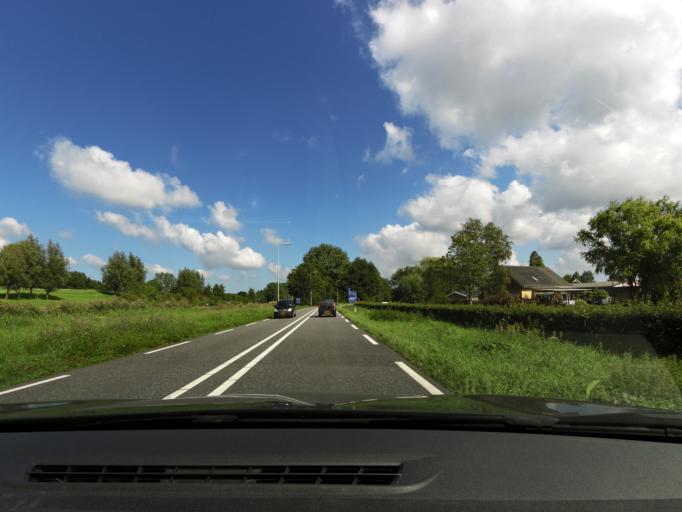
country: NL
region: South Holland
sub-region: Gemeente Alphen aan den Rijn
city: Alphen aan den Rijn
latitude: 52.1400
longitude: 4.6983
